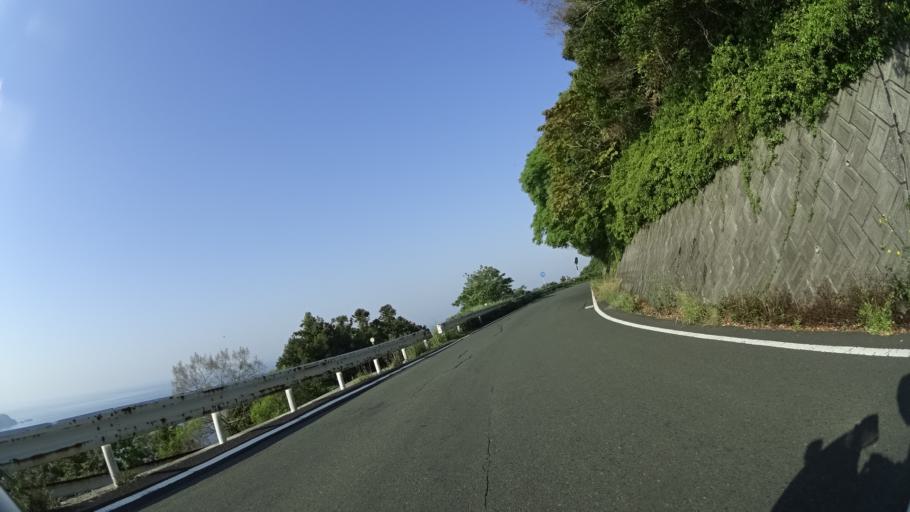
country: JP
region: Ehime
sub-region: Nishiuwa-gun
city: Ikata-cho
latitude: 33.3846
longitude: 132.0873
